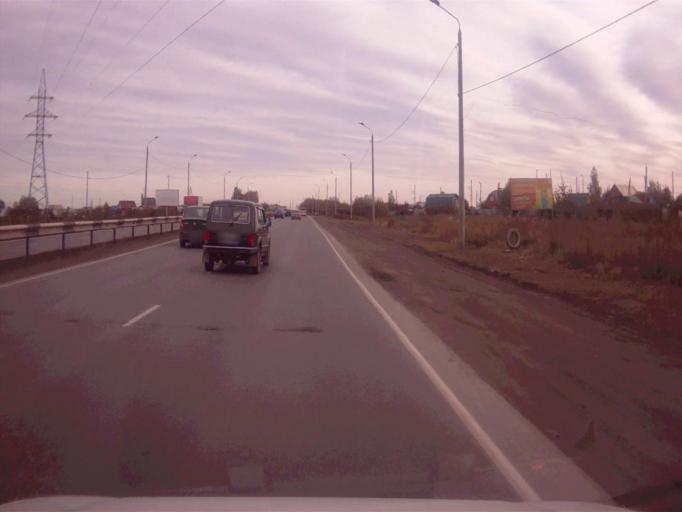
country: RU
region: Chelyabinsk
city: Novosineglazovskiy
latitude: 55.0452
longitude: 61.4206
